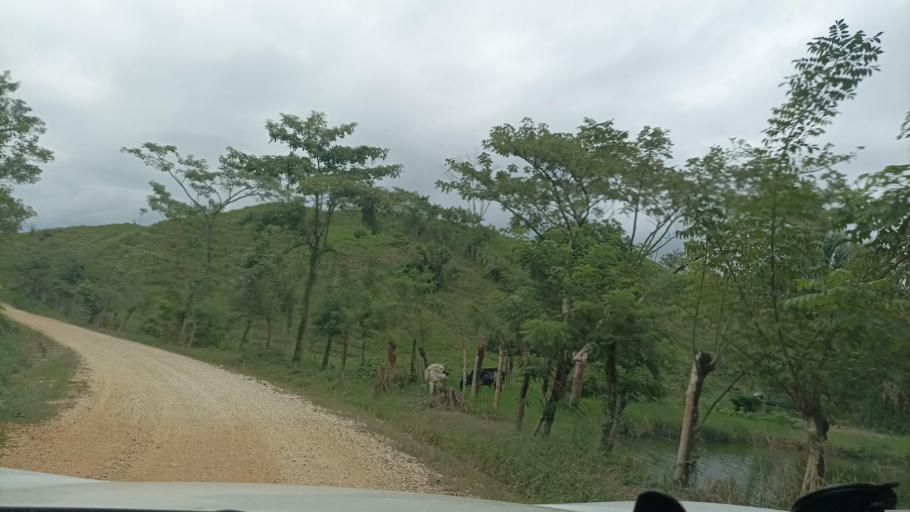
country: MX
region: Veracruz
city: Hidalgotitlan
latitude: 17.6240
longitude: -94.5122
